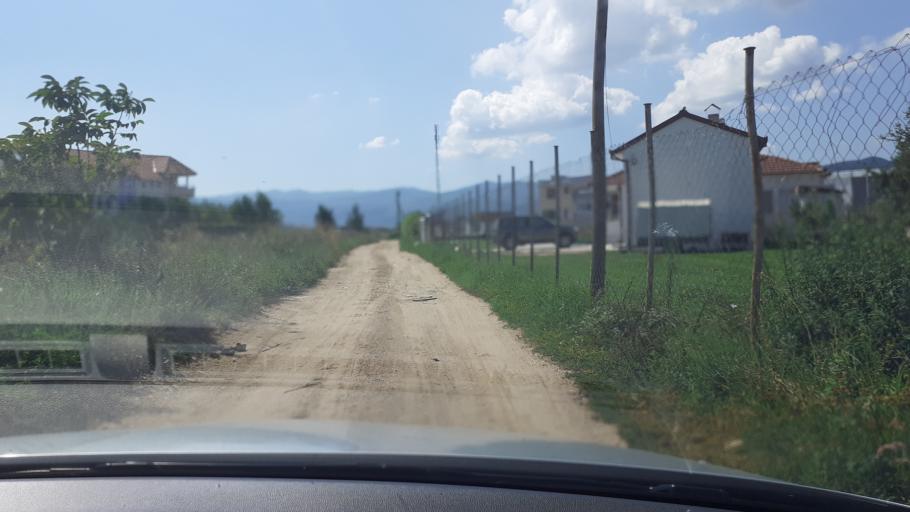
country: MK
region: Vasilevo
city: Vasilevo
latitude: 41.4685
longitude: 22.6425
